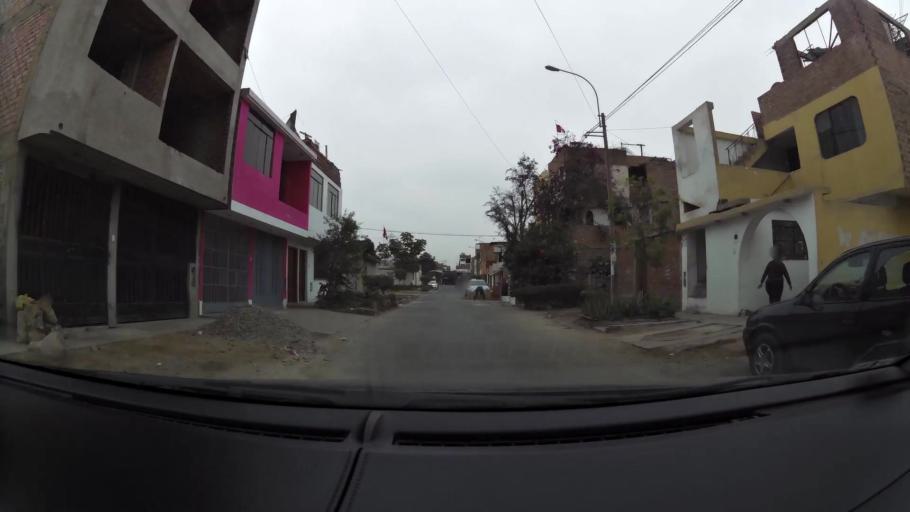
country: PE
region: Lima
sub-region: Lima
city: Independencia
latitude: -11.9422
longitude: -77.0862
